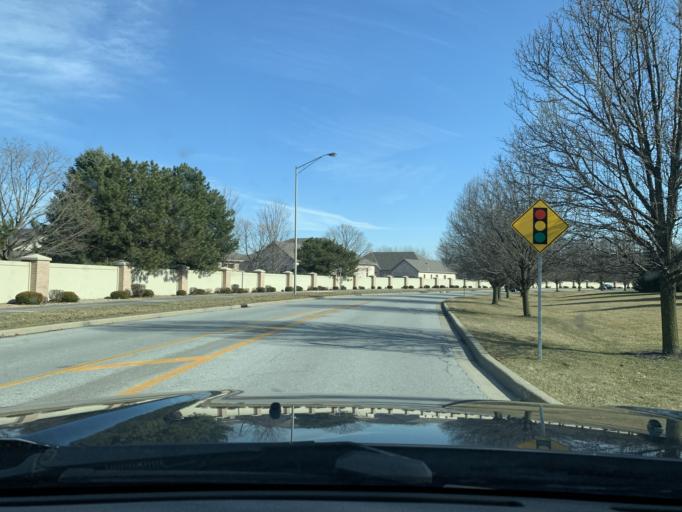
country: US
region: Indiana
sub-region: Lake County
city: Dyer
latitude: 41.5249
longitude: -87.4881
